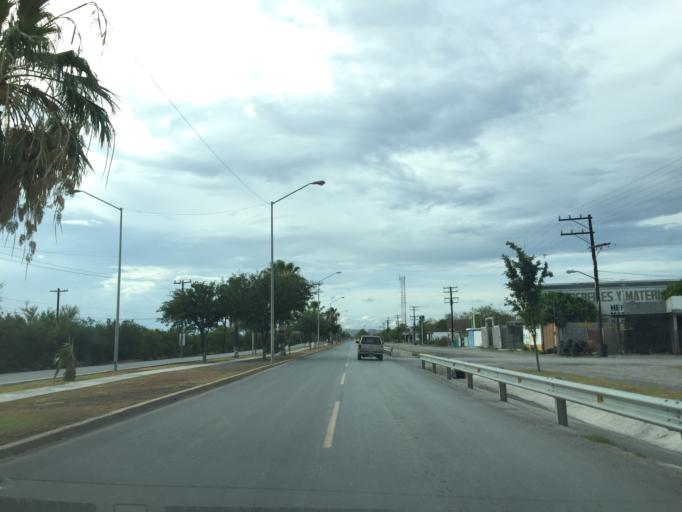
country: MX
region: Nuevo Leon
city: Marin
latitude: 25.8596
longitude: -100.0239
